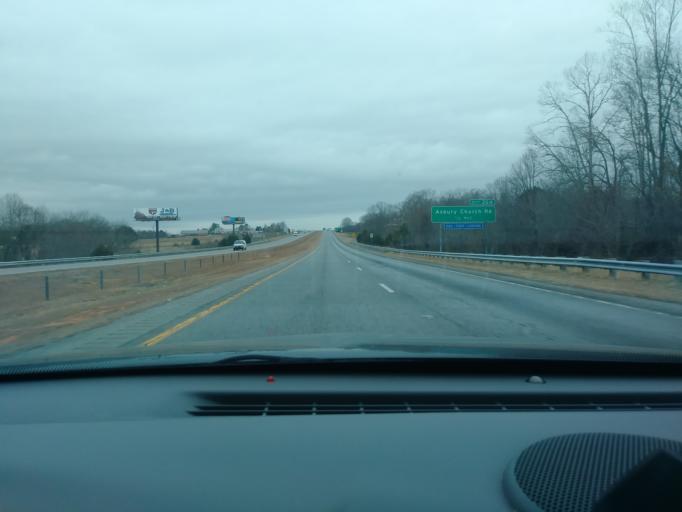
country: US
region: North Carolina
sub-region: Yadkin County
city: Yadkinville
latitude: 36.1175
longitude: -80.7802
